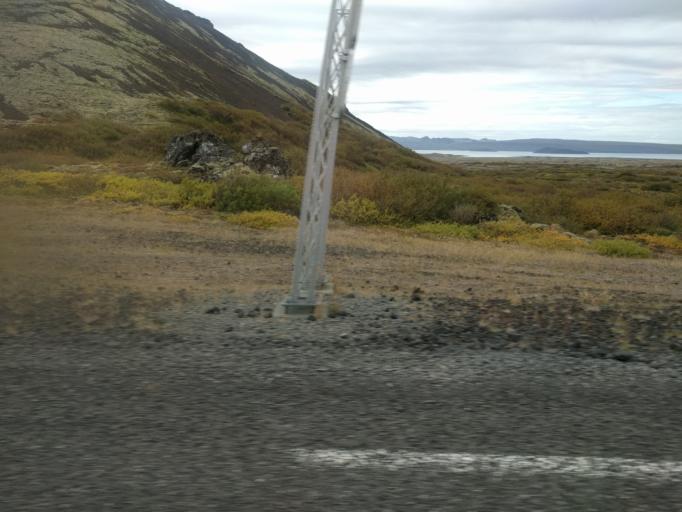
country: IS
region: South
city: Hveragerdi
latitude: 64.1983
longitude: -21.0304
